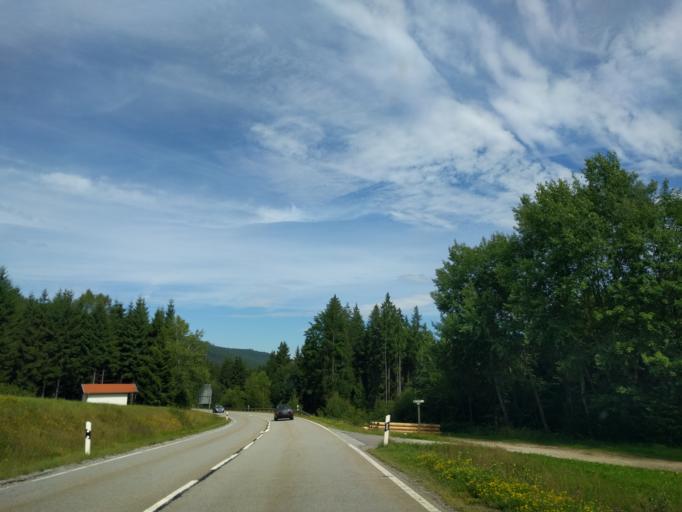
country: DE
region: Bavaria
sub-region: Lower Bavaria
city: Langdorf
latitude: 49.0175
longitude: 13.1417
